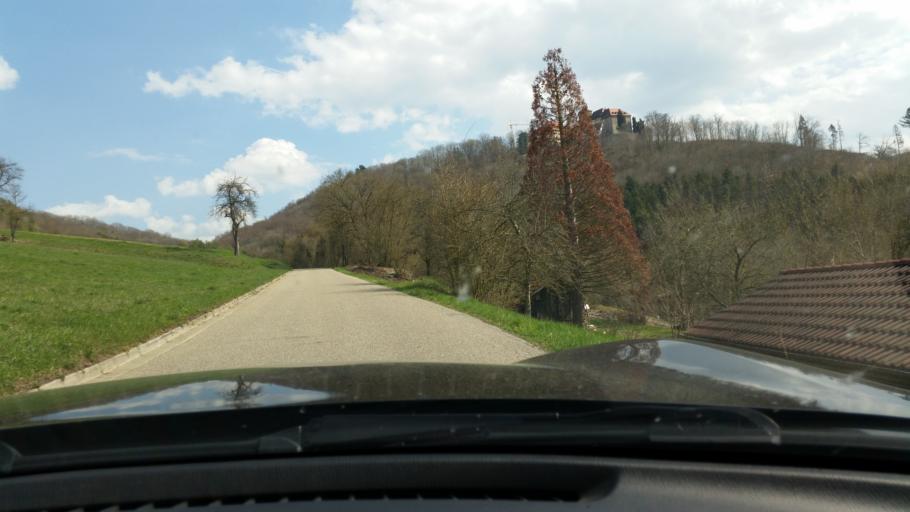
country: DE
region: Baden-Wuerttemberg
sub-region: Regierungsbezirk Stuttgart
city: Braunsbach
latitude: 49.2691
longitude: 9.7625
